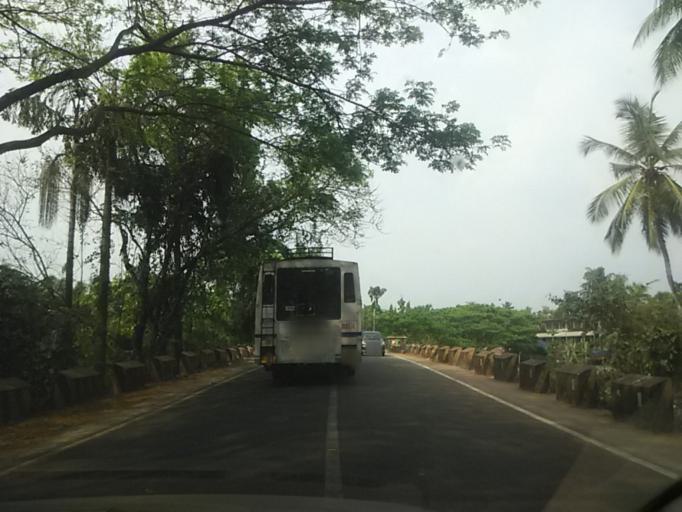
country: IN
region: Kerala
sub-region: Kozhikode
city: Naduvannur
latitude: 11.4657
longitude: 75.7720
